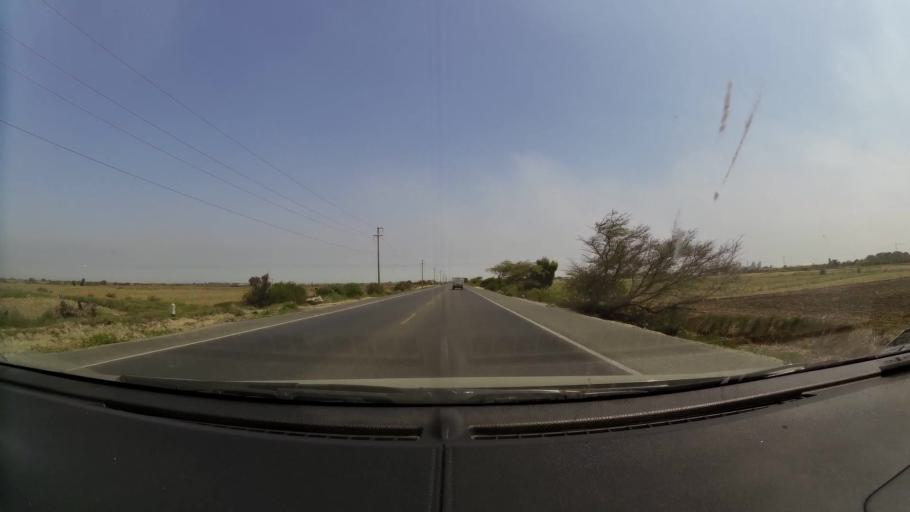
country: PE
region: La Libertad
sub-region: Provincia de Pacasmayo
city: San Pedro de Lloc
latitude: -7.4189
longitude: -79.5336
